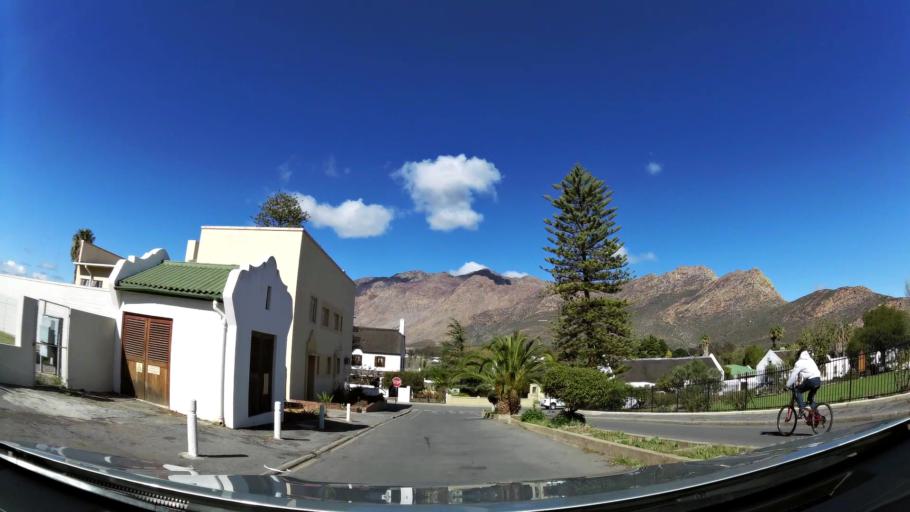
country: ZA
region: Western Cape
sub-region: Cape Winelands District Municipality
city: Ashton
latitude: -33.7867
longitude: 20.1195
